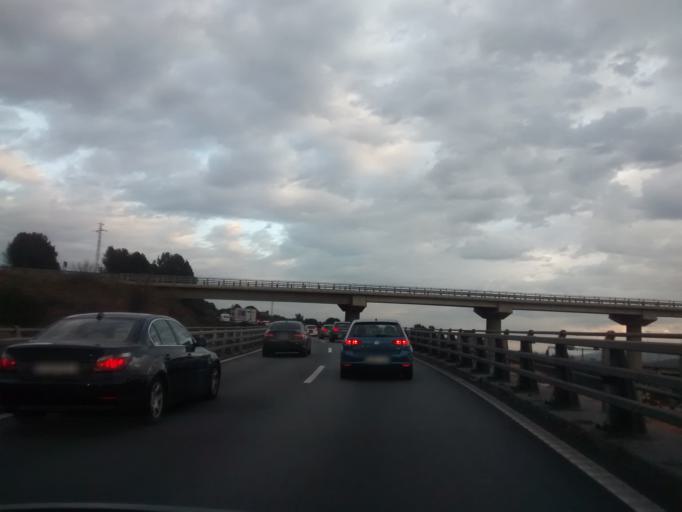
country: ES
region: Catalonia
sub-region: Provincia de Barcelona
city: Palleja
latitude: 41.4479
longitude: 1.9971
